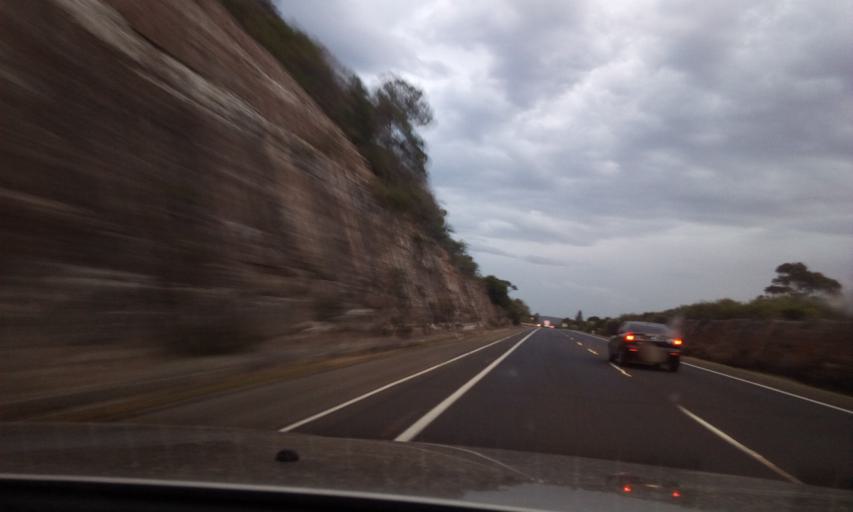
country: AU
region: New South Wales
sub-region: Wollongong
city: Bulli
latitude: -34.2585
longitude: 150.9310
